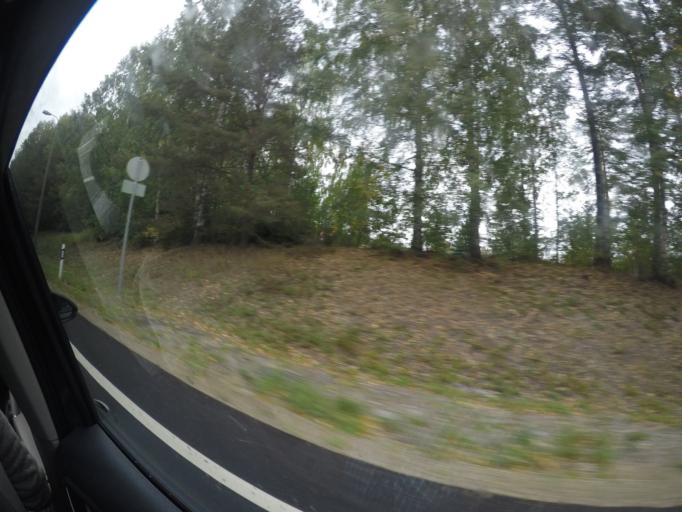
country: FI
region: Pirkanmaa
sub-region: Tampere
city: Kangasala
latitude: 61.4474
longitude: 24.1059
